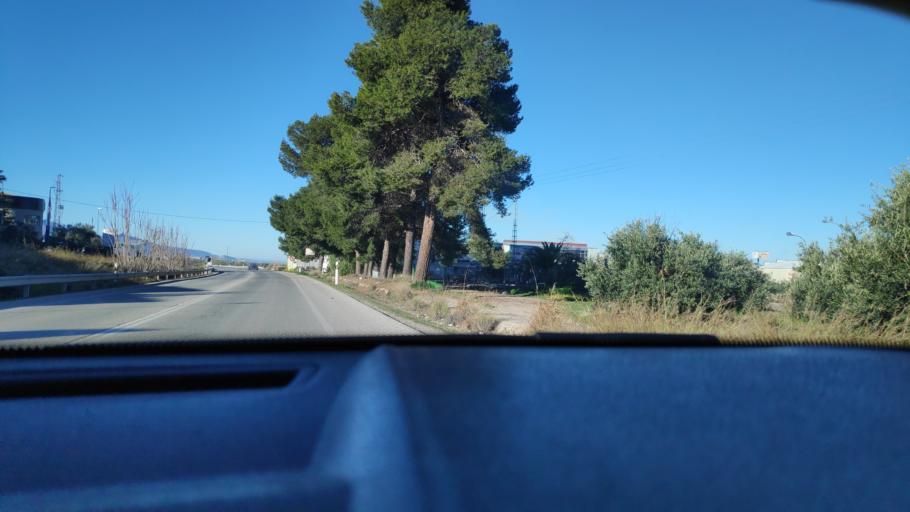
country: ES
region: Andalusia
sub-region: Provincia de Jaen
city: Mancha Real
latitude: 37.8065
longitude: -3.6164
